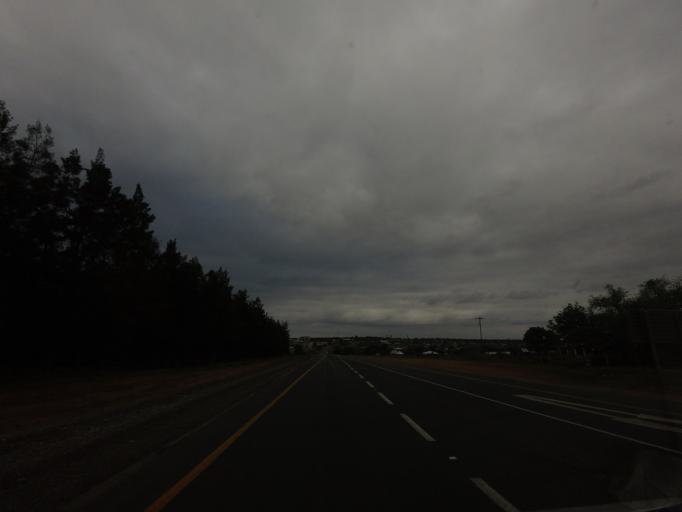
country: ZA
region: Mpumalanga
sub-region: Ehlanzeni District
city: Komatipoort
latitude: -25.4479
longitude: 31.6704
